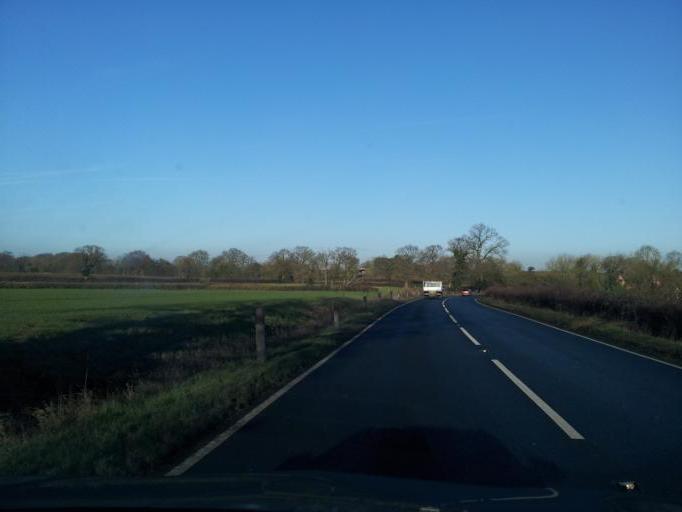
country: GB
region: England
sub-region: Suffolk
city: Lavenham
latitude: 52.1525
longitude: 0.7577
